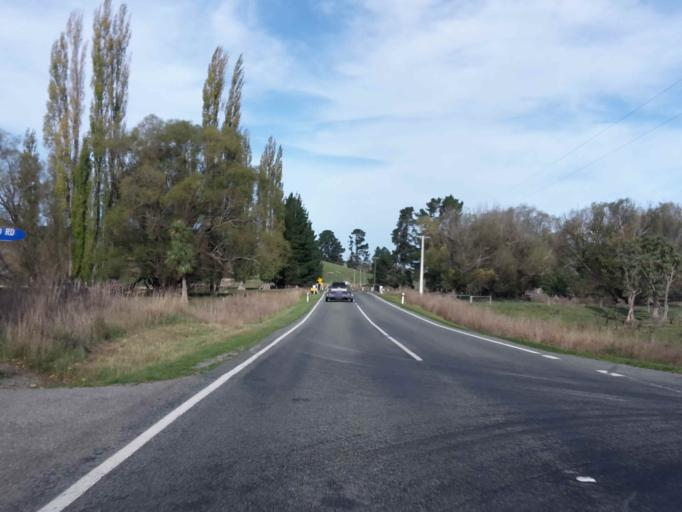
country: NZ
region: Canterbury
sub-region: Timaru District
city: Pleasant Point
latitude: -44.0633
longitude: 170.9408
